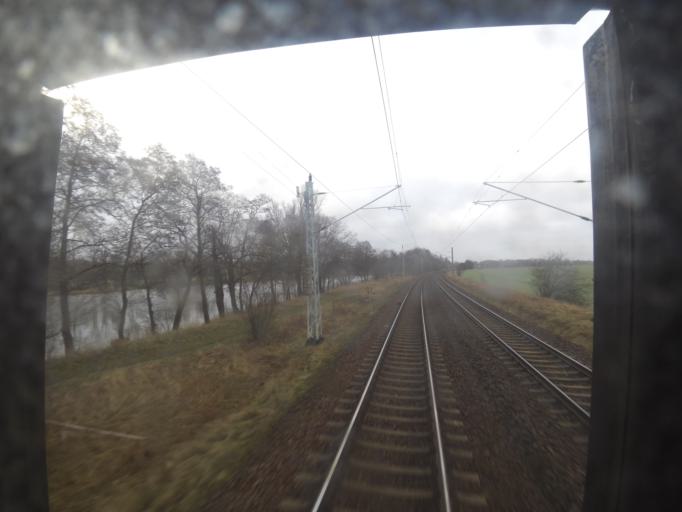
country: DE
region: Brandenburg
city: Rangsdorf
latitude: 52.2776
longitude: 13.4362
